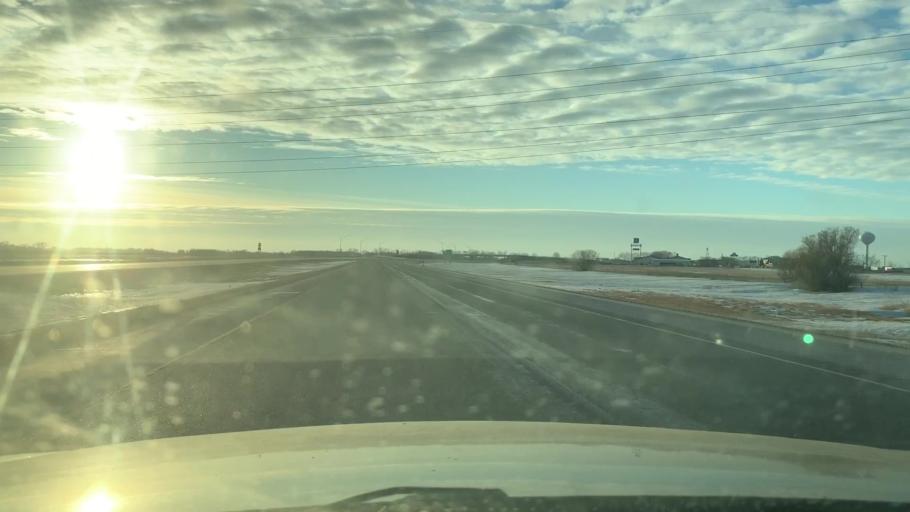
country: US
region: North Dakota
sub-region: Cass County
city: Casselton
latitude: 46.8756
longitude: -97.1997
